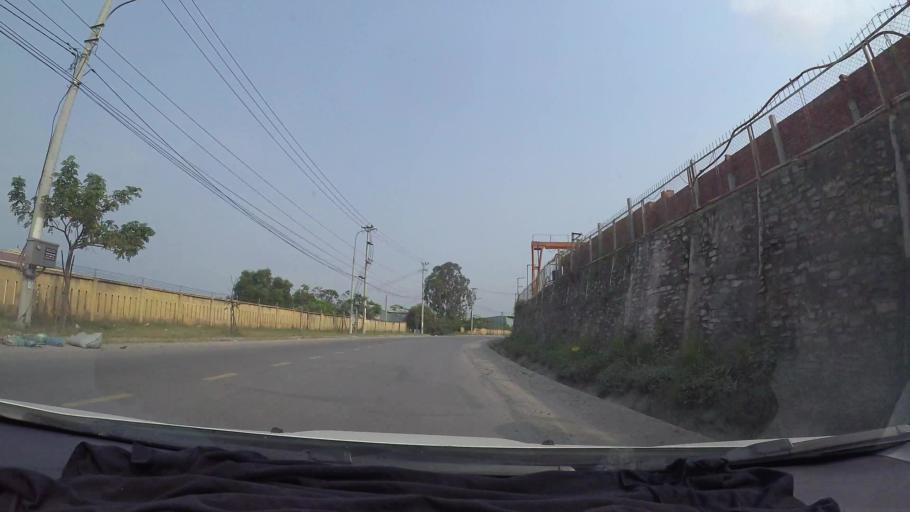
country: VN
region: Da Nang
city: Lien Chieu
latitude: 16.0387
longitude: 108.1719
